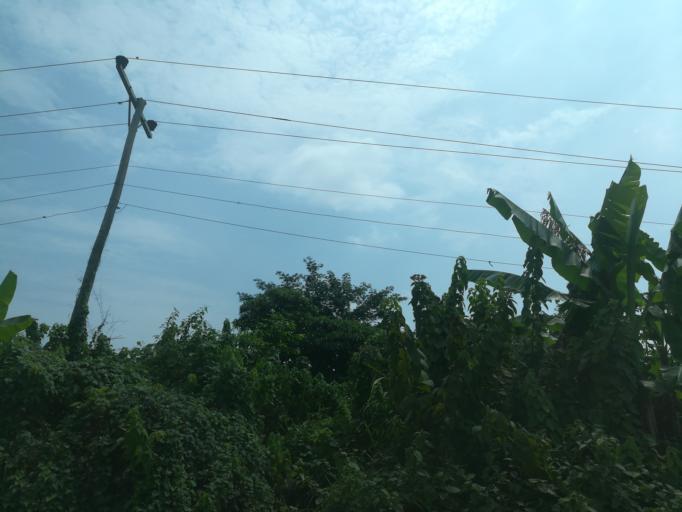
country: NG
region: Lagos
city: Ikorodu
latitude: 6.5977
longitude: 3.6309
